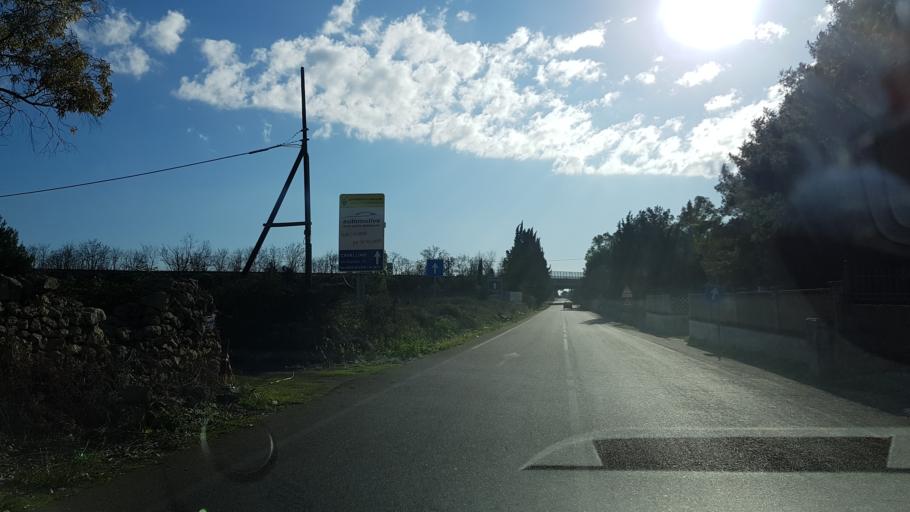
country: IT
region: Apulia
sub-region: Provincia di Lecce
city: Castromediano
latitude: 40.3278
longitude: 18.1835
